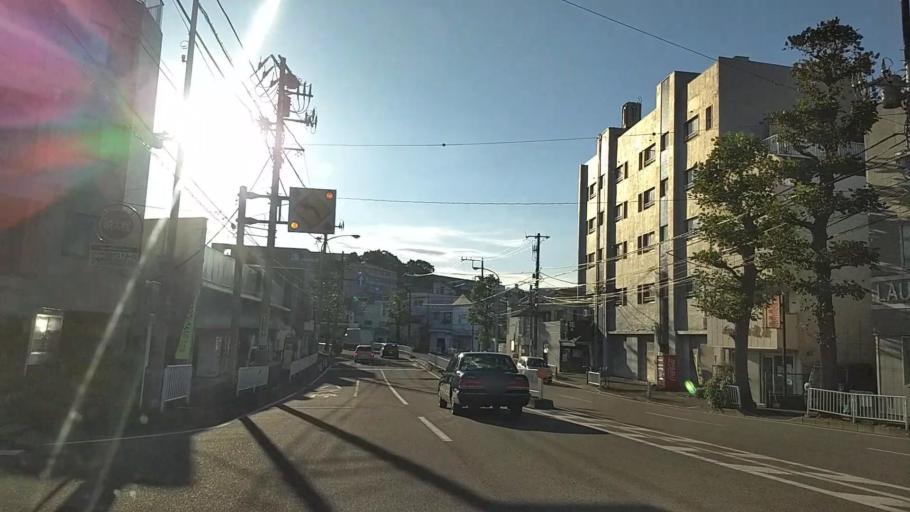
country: JP
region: Kanagawa
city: Yokohama
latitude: 35.4517
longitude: 139.6221
